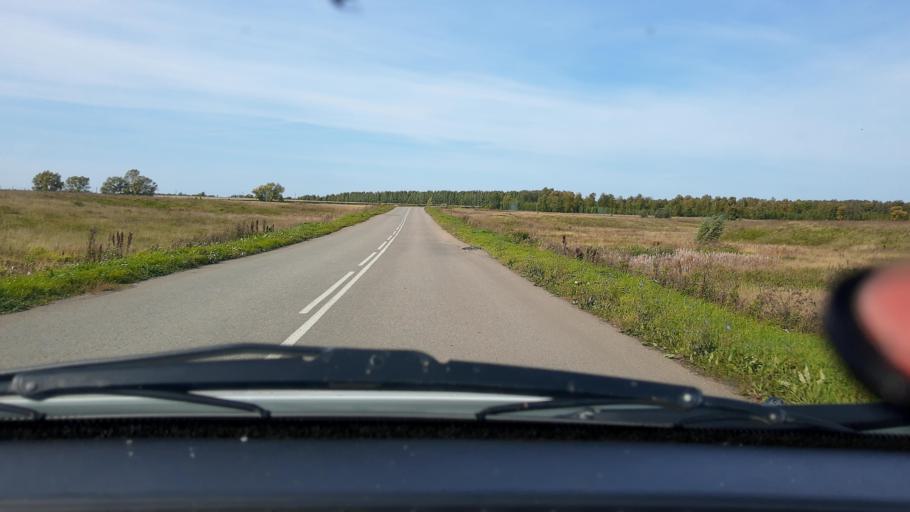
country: RU
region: Bashkortostan
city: Iglino
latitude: 54.7796
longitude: 56.5467
